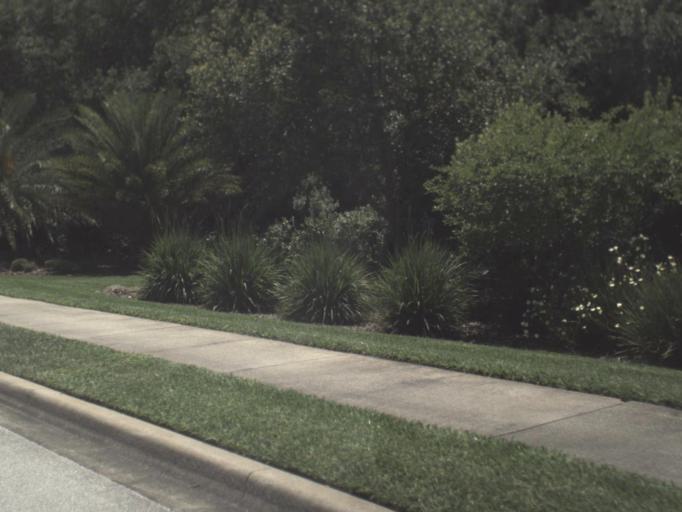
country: US
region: Florida
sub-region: Saint Johns County
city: Saint Augustine Beach
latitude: 29.8331
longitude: -81.2742
